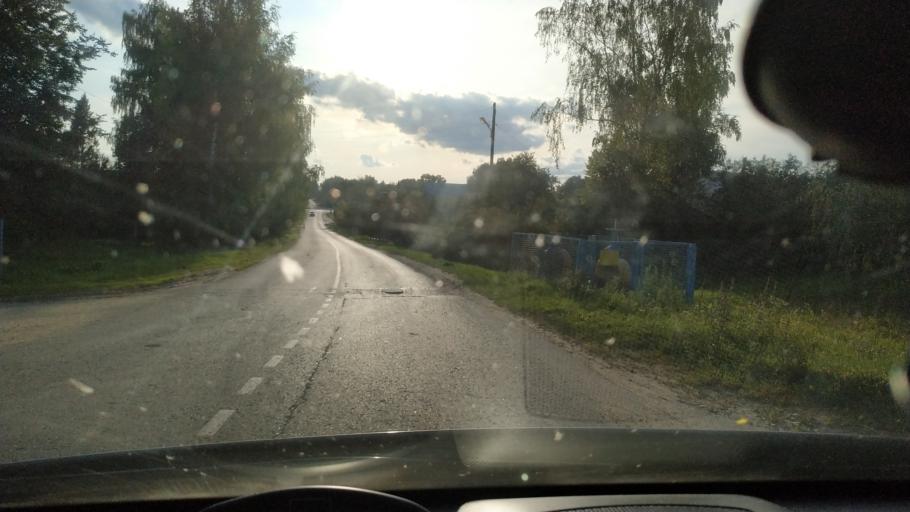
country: RU
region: Rjazan
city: Solotcha
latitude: 54.8667
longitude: 39.6551
